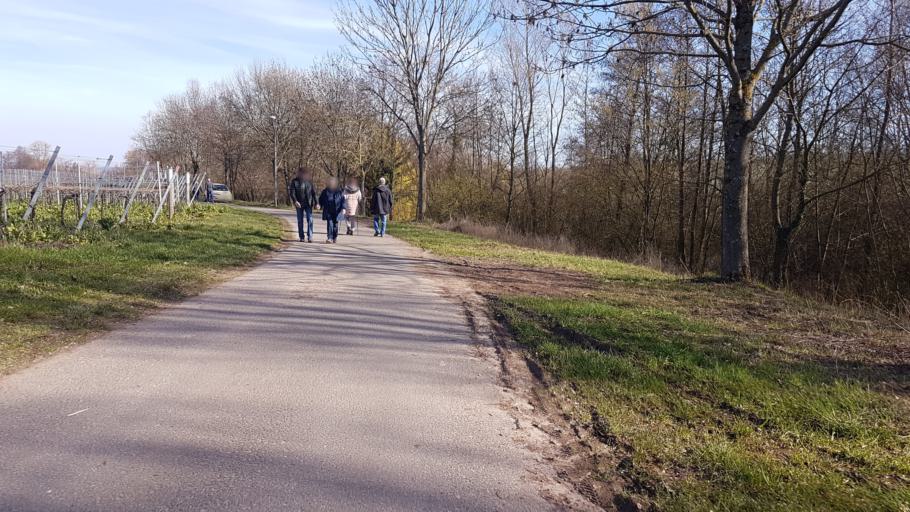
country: DE
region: Rheinland-Pfalz
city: Sankt Martin
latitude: 49.2988
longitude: 8.1144
